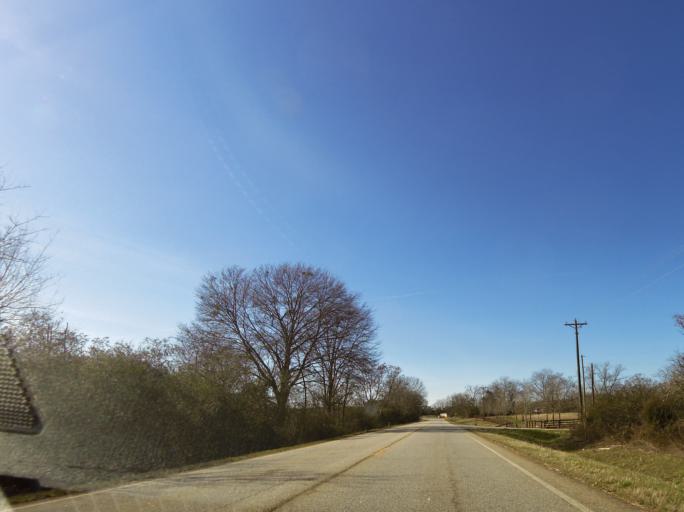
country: US
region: Georgia
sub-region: Crawford County
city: Roberta
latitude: 32.8765
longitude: -84.0735
